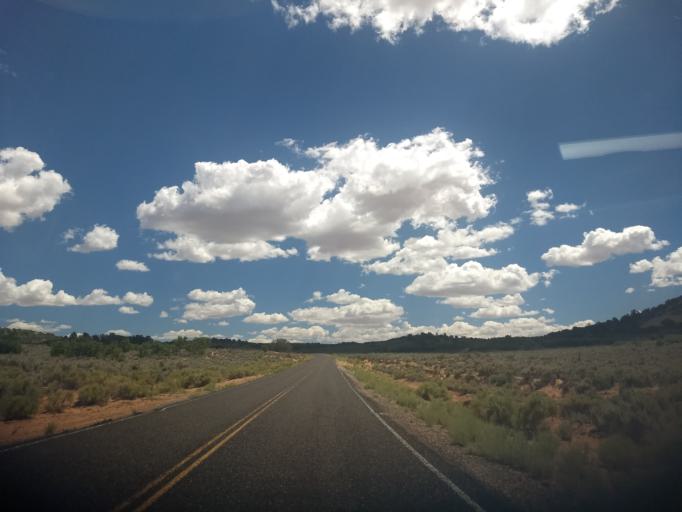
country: US
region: Utah
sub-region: Kane County
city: Kanab
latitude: 37.1365
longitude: -112.6760
